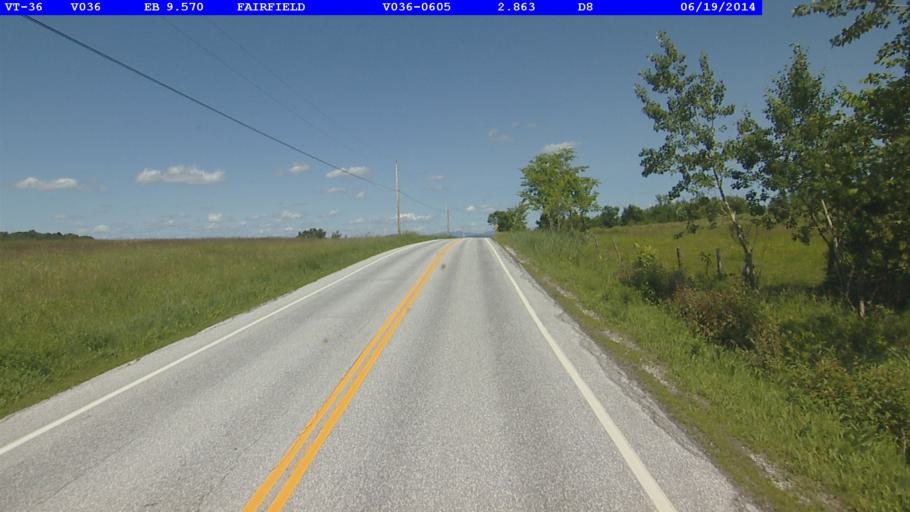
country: US
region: Vermont
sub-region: Franklin County
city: Saint Albans
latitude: 44.7936
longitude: -72.9756
